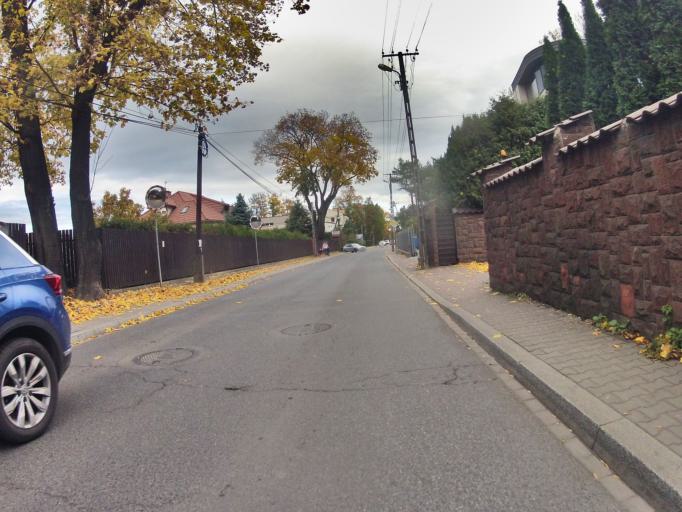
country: PL
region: Lesser Poland Voivodeship
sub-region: Powiat krakowski
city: Rzaska
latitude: 50.0669
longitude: 19.8744
